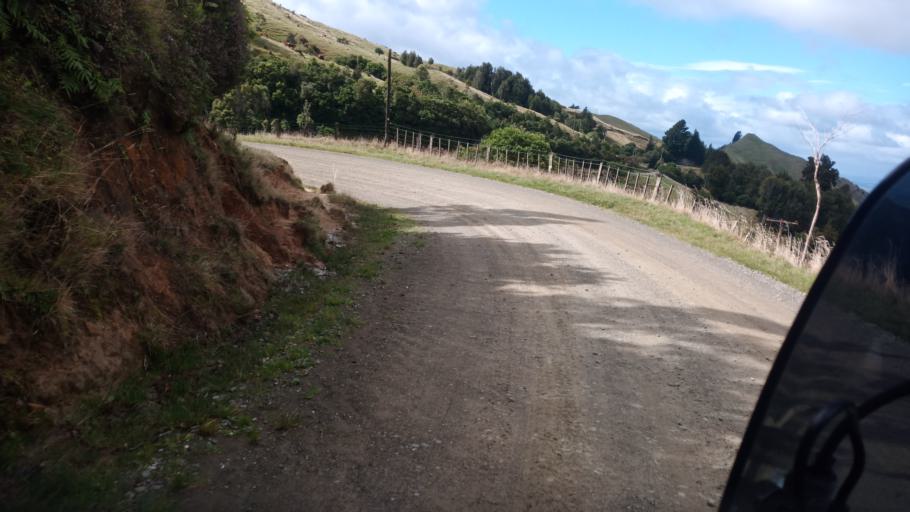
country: NZ
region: Gisborne
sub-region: Gisborne District
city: Gisborne
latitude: -38.4848
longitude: 177.5980
